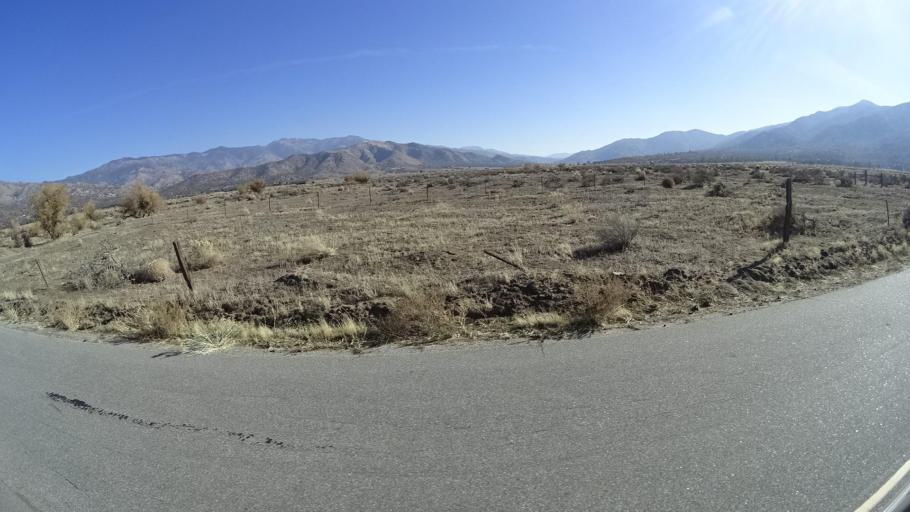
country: US
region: California
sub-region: Kern County
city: Bodfish
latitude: 35.4073
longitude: -118.5247
